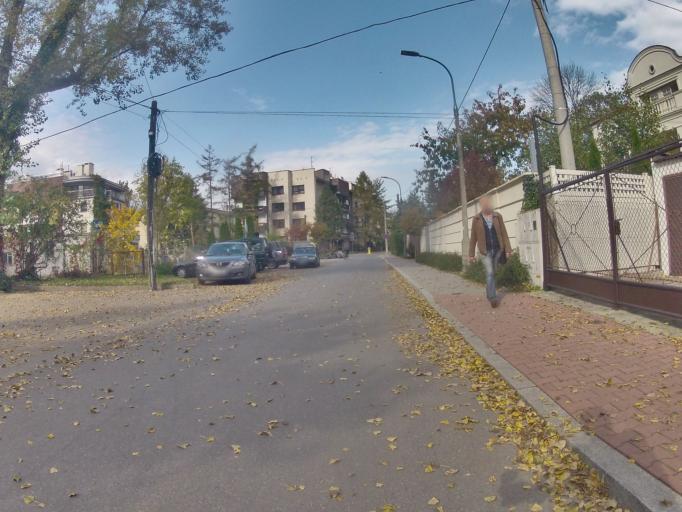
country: PL
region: Lesser Poland Voivodeship
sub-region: Krakow
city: Krakow
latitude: 50.0557
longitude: 19.9138
